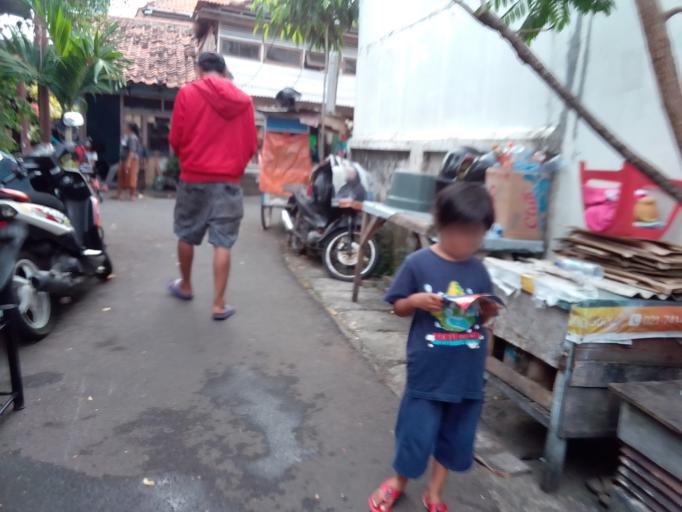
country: ID
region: Jakarta Raya
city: Jakarta
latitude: -6.1719
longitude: 106.8163
